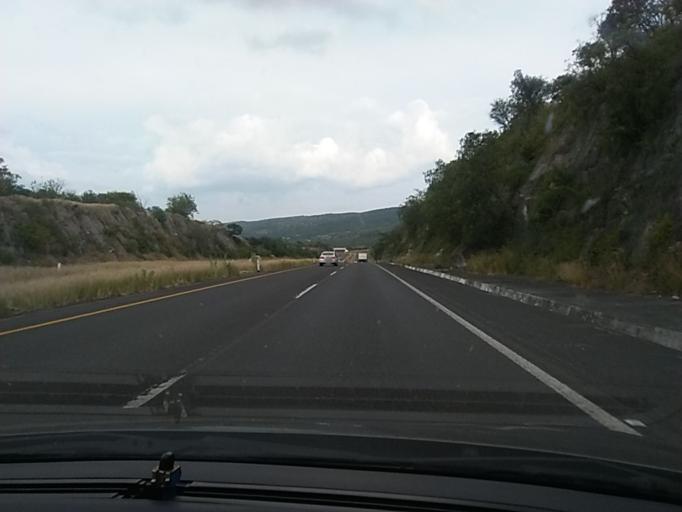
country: MX
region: Mexico
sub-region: Chapultepec
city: Chucandiro
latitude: 19.8876
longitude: -101.3217
